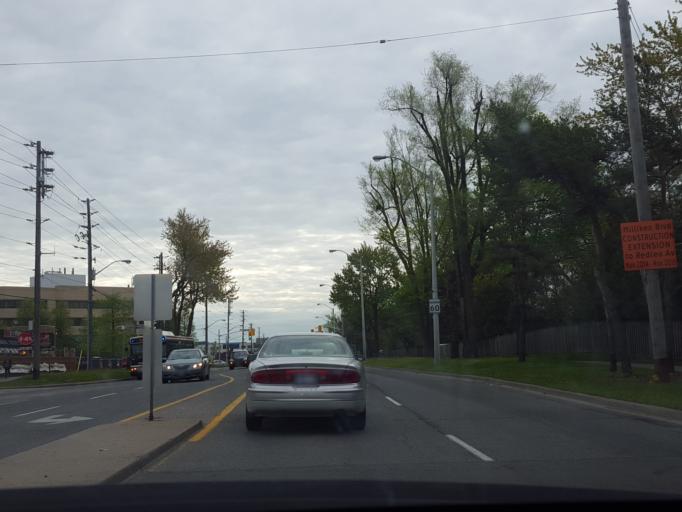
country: CA
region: Ontario
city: Scarborough
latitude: 43.8013
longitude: -79.2962
